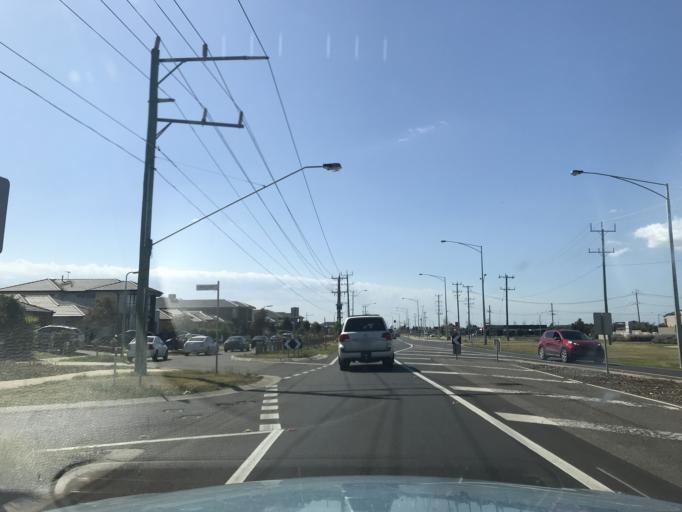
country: AU
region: Victoria
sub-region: Wyndham
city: Williams Landing
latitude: -37.8524
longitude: 144.7286
